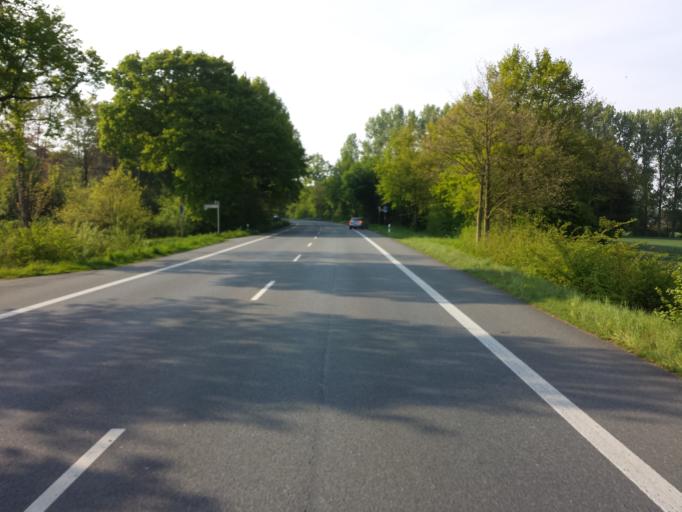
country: DE
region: North Rhine-Westphalia
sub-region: Regierungsbezirk Detmold
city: Guetersloh
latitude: 51.9382
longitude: 8.3540
